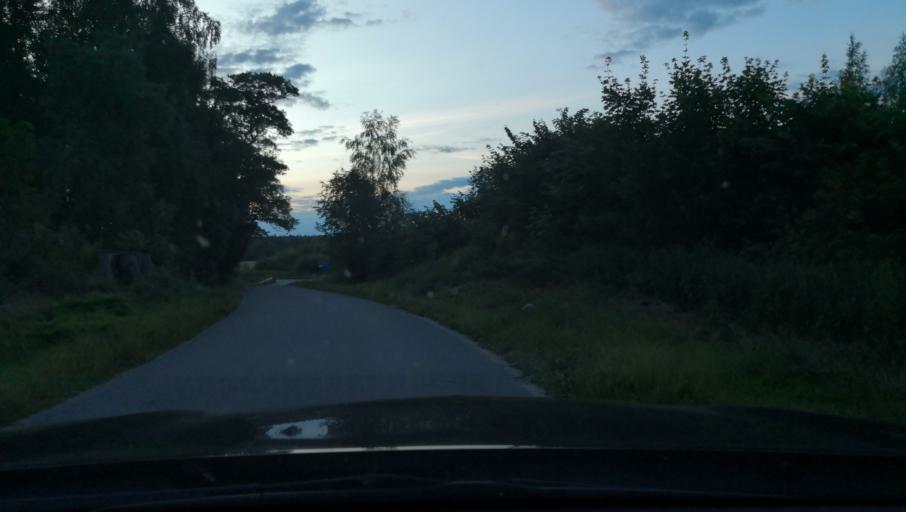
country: SE
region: Uppsala
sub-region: Osthammars Kommun
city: Bjorklinge
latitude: 60.0622
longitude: 17.5799
